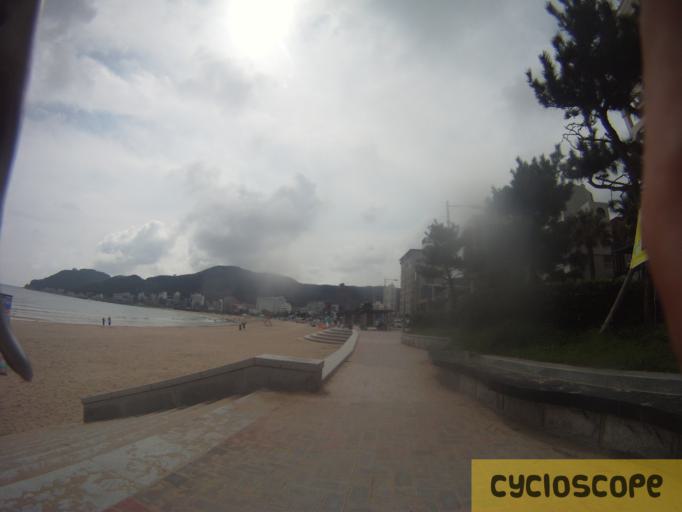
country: KR
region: Busan
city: Kijang
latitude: 35.1799
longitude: 129.2009
